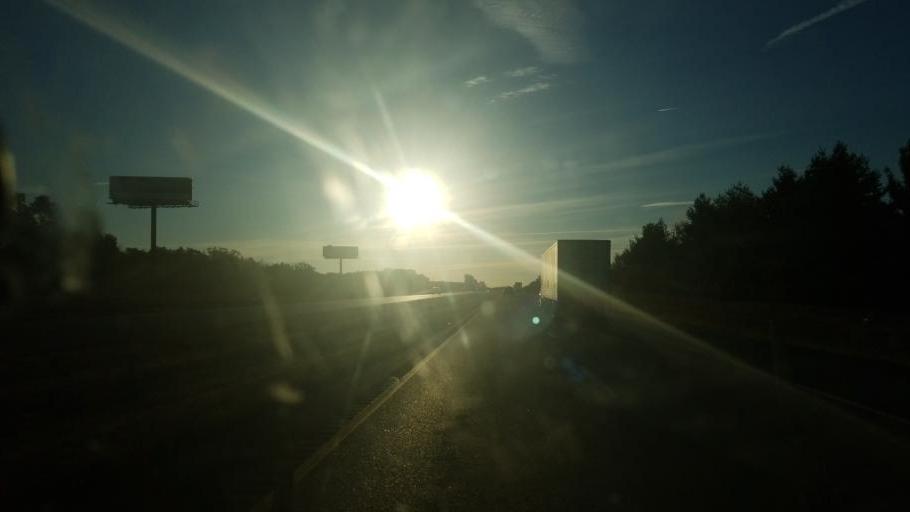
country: US
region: Missouri
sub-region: Montgomery County
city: Montgomery City
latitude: 38.9016
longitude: -91.6403
